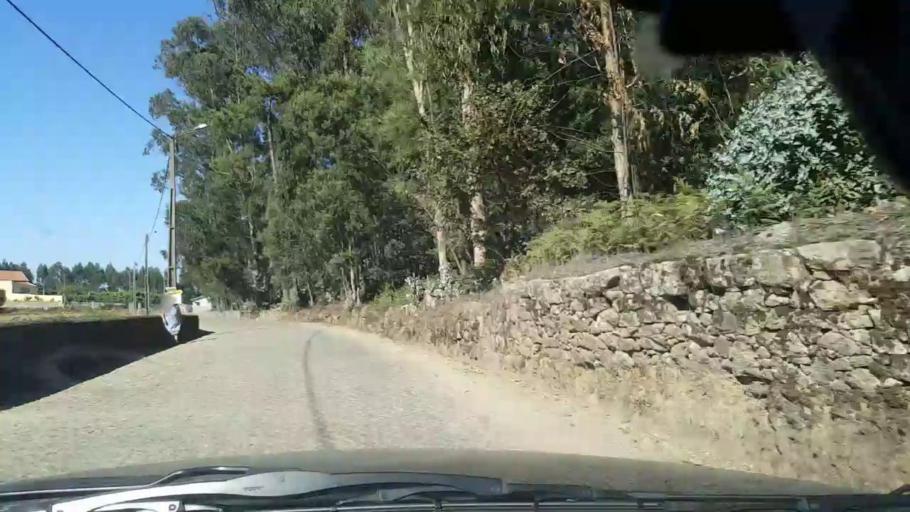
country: PT
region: Braga
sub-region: Vila Nova de Famalicao
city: Ribeirao
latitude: 41.3775
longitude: -8.6377
